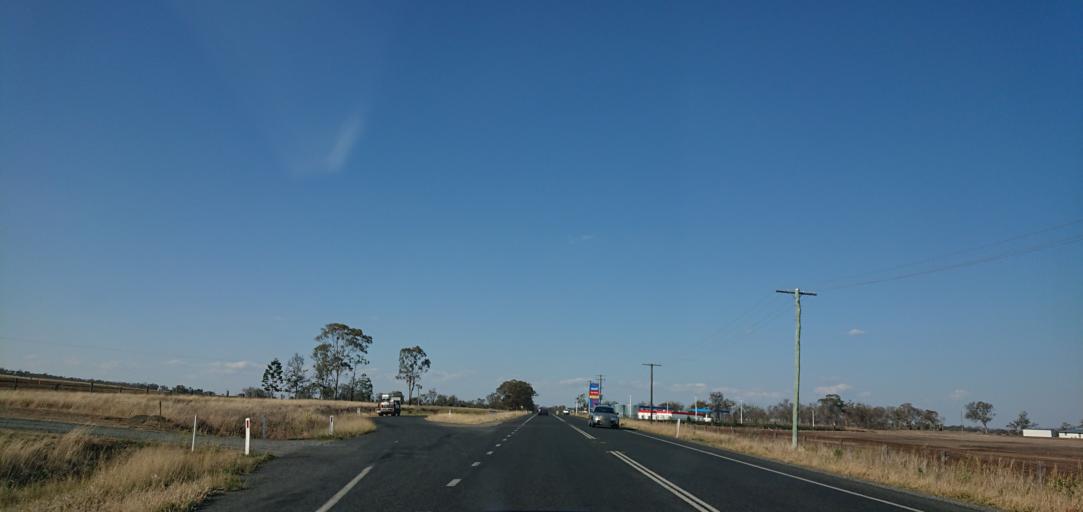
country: AU
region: Queensland
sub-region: Toowoomba
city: Westbrook
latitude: -27.6386
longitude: 151.7407
